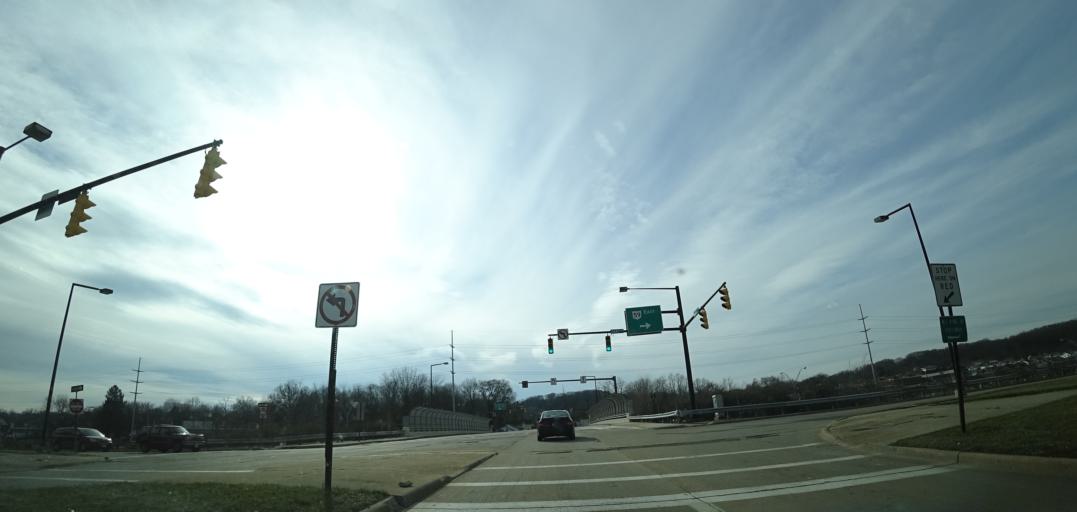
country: US
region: Ohio
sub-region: Summit County
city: Akron
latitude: 41.0706
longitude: -81.5368
